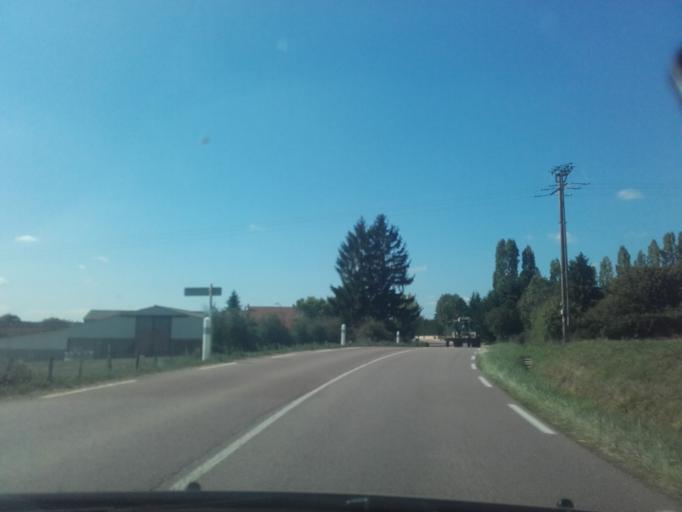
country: FR
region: Bourgogne
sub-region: Departement de la Cote-d'Or
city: Nolay
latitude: 46.9430
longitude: 4.6527
